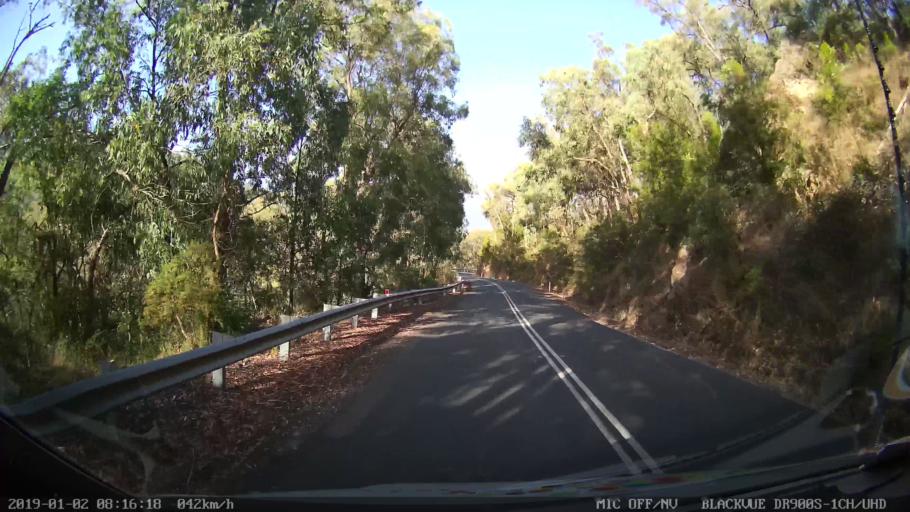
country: AU
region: New South Wales
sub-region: Tumut Shire
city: Tumut
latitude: -35.5802
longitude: 148.3318
